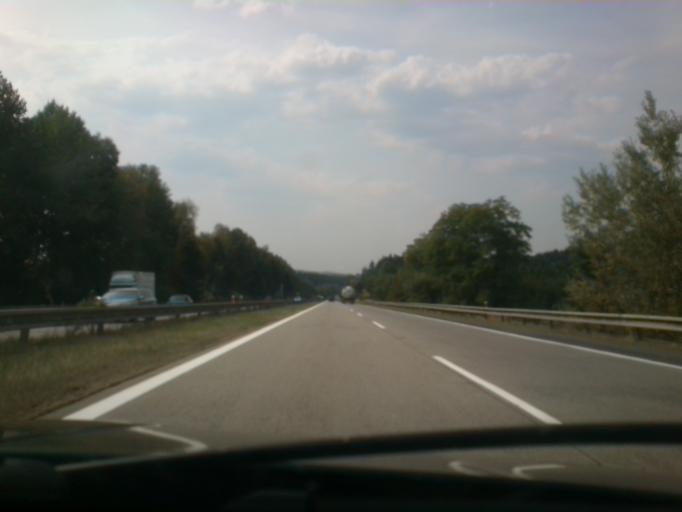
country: CZ
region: Central Bohemia
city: Divisov
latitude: 49.8056
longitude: 14.8975
